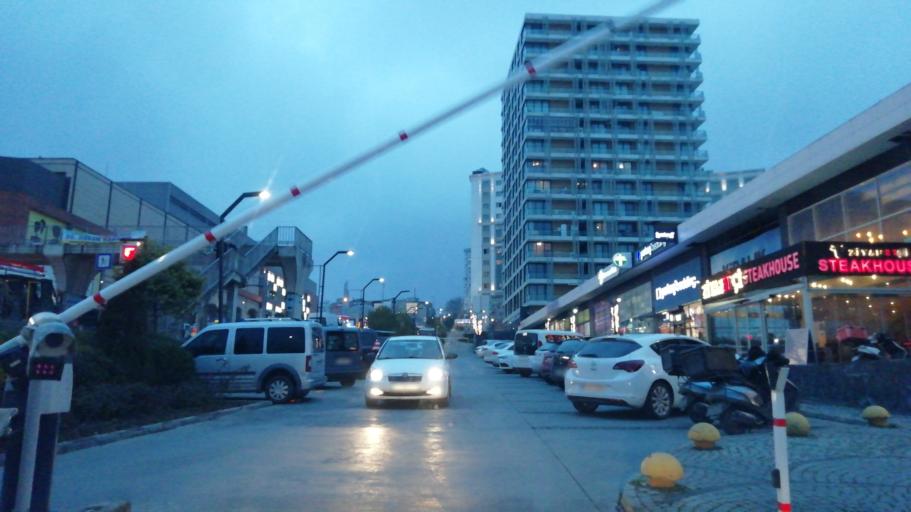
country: TR
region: Istanbul
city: Mahmutbey
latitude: 41.0099
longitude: 28.8153
